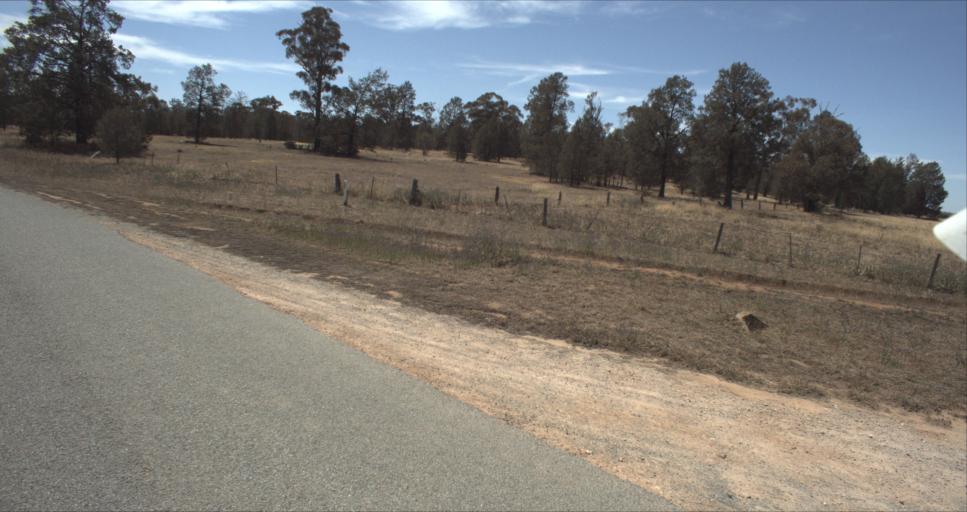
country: AU
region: New South Wales
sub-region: Leeton
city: Leeton
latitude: -34.6733
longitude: 146.4443
